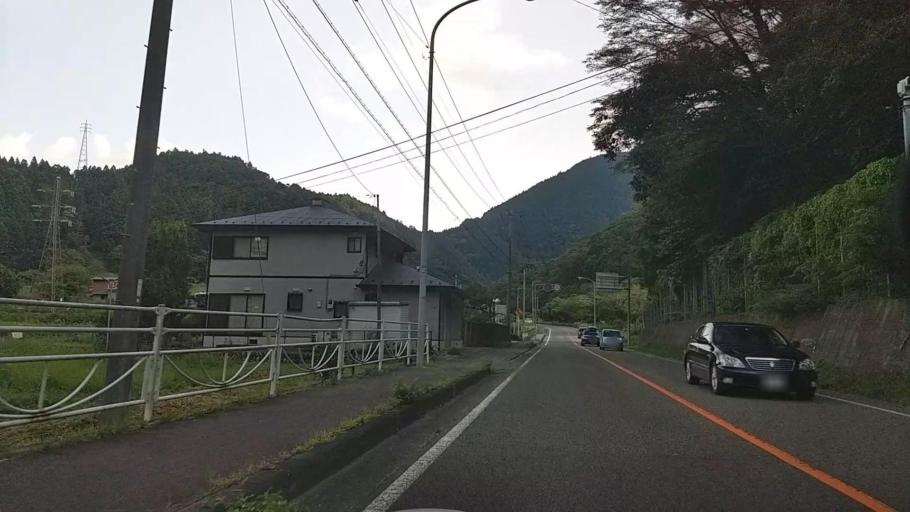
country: JP
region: Shizuoka
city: Fujinomiya
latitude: 35.3326
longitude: 138.4267
